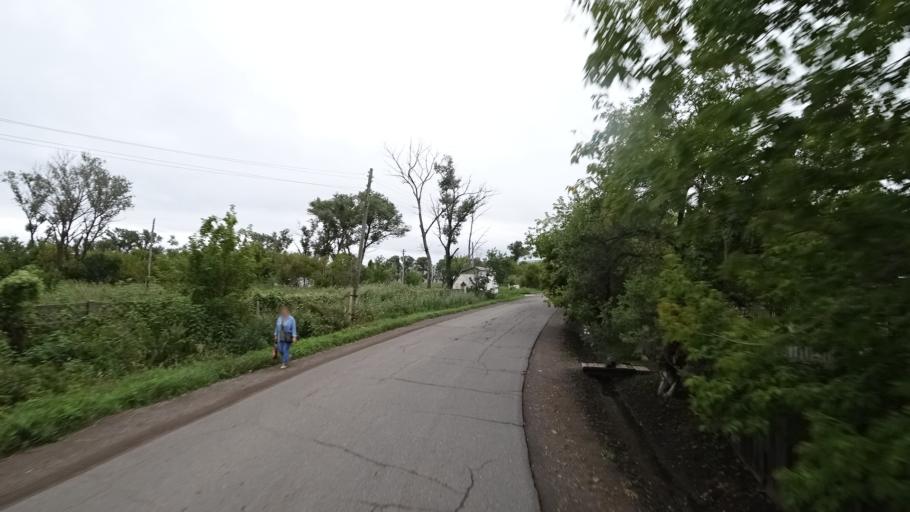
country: RU
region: Primorskiy
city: Chernigovka
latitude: 44.3334
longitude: 132.5322
